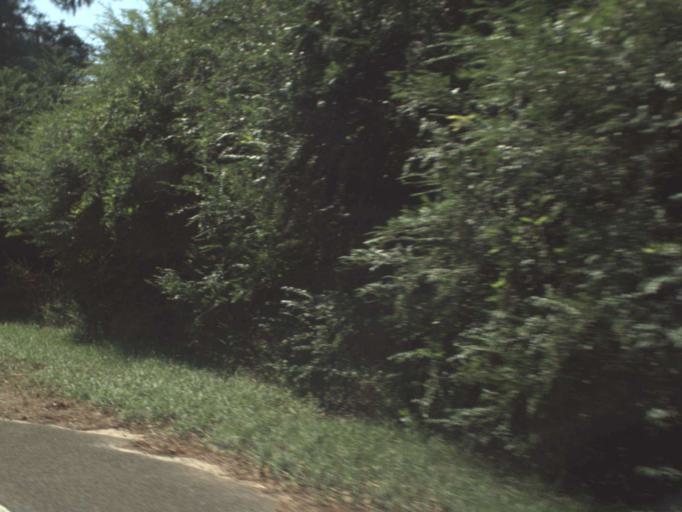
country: US
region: Florida
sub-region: Walton County
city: DeFuniak Springs
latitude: 30.9247
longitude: -86.1371
